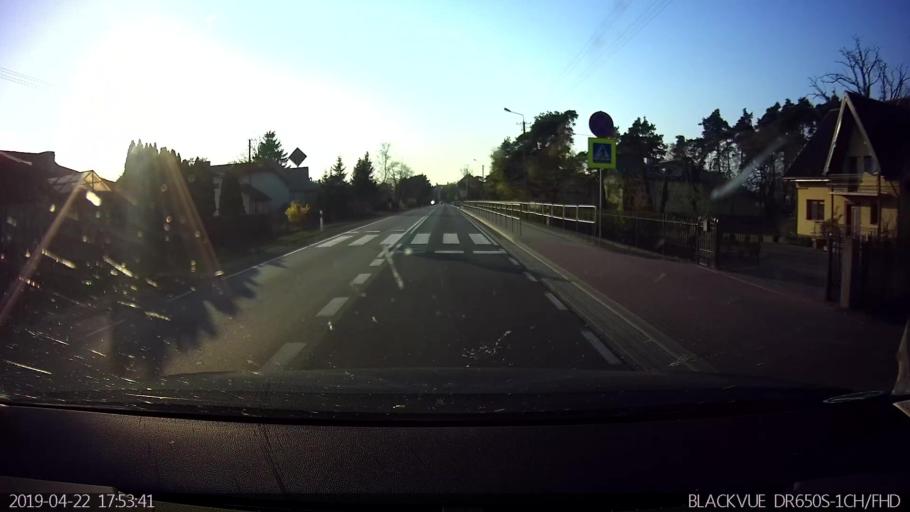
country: PL
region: Masovian Voivodeship
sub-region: Powiat wegrowski
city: Liw
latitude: 52.4547
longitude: 21.9507
